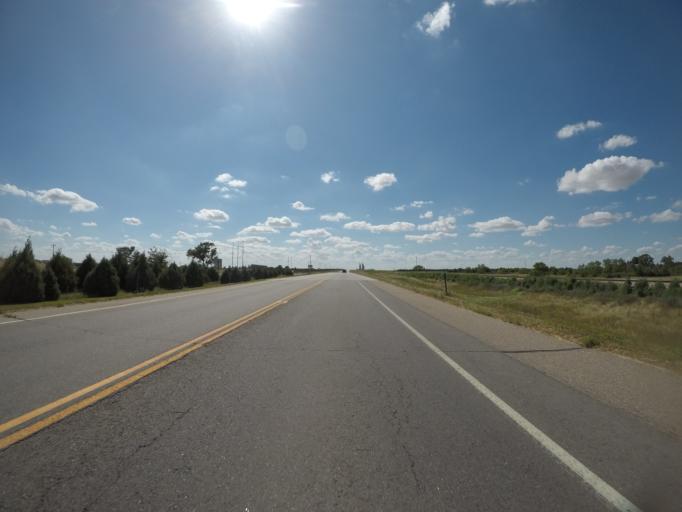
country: US
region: Colorado
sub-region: Phillips County
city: Holyoke
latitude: 40.5867
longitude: -102.3194
